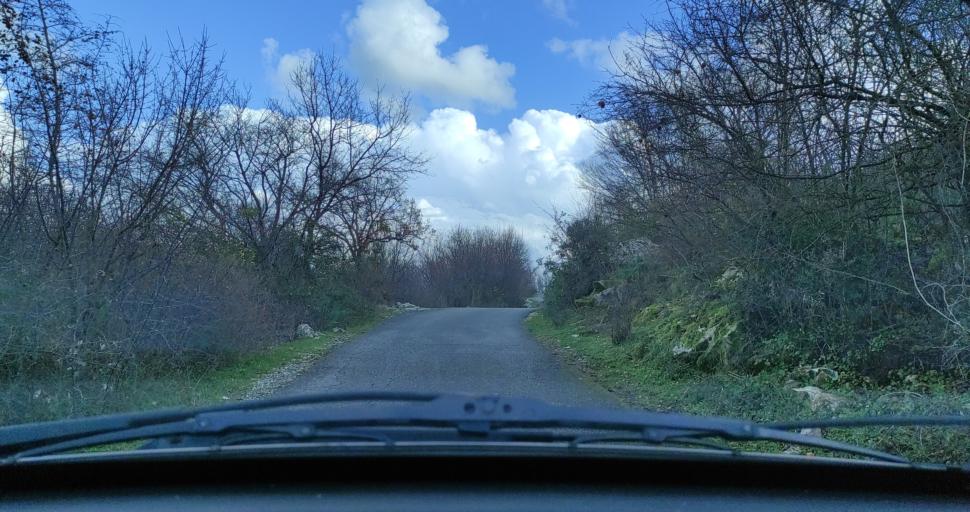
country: AL
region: Shkoder
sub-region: Rrethi i Shkodres
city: Dajc
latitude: 42.0702
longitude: 19.4045
